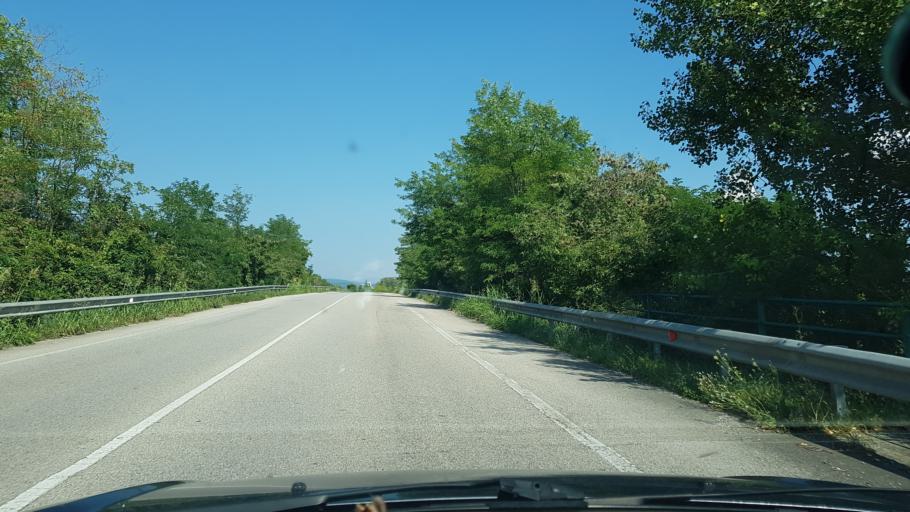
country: IT
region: Friuli Venezia Giulia
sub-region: Provincia di Gorizia
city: Staranzano
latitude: 45.7941
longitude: 13.4932
